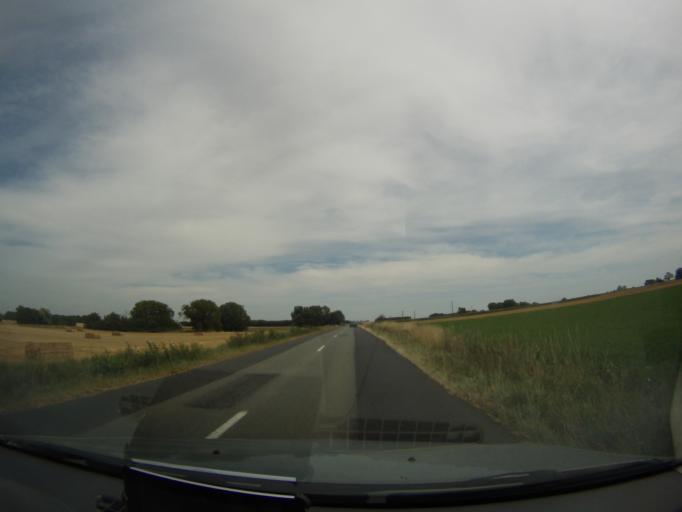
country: FR
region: Poitou-Charentes
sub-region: Departement de la Vienne
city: Mirebeau
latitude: 46.7605
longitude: 0.1581
